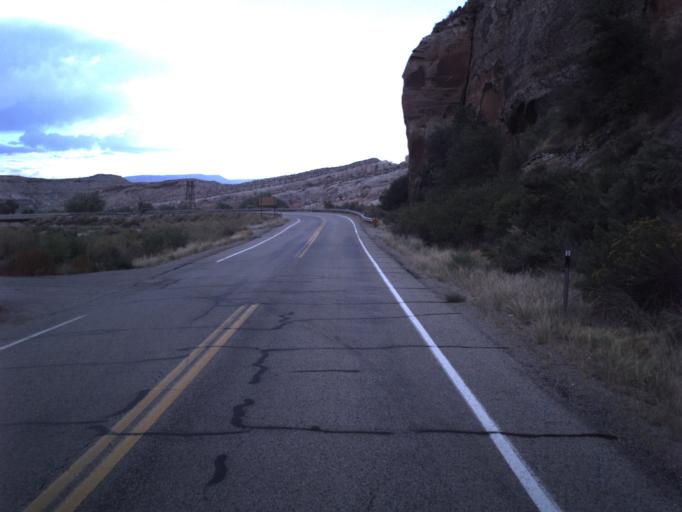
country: US
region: Utah
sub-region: Grand County
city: Moab
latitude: 38.8103
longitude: -109.3079
